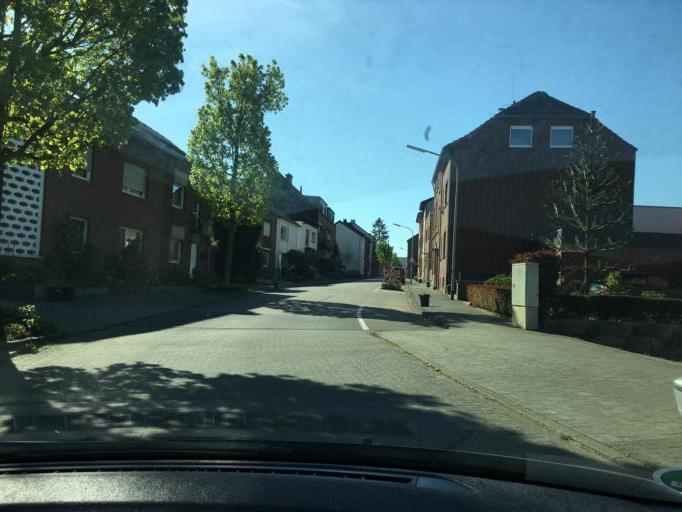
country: DE
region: North Rhine-Westphalia
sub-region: Regierungsbezirk Dusseldorf
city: Monchengladbach
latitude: 51.1782
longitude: 6.4267
